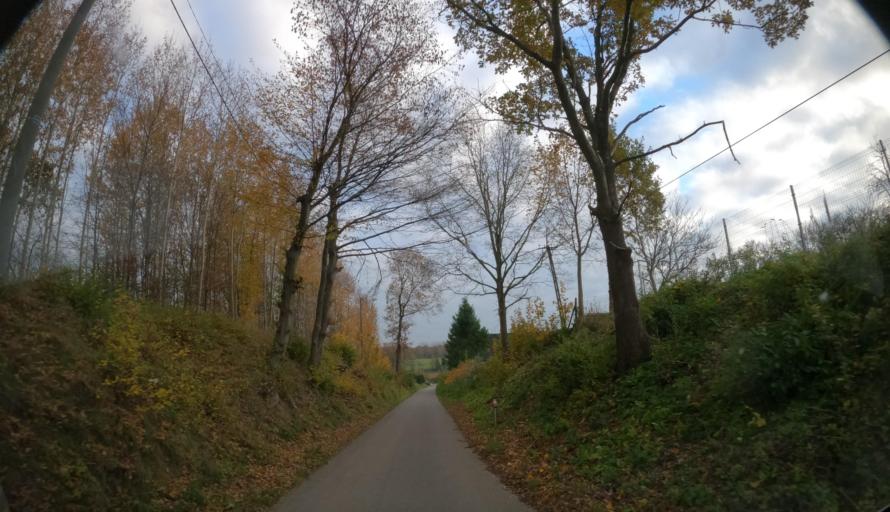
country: PL
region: Pomeranian Voivodeship
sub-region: Powiat slupski
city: Kepice
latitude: 54.2570
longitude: 16.9376
